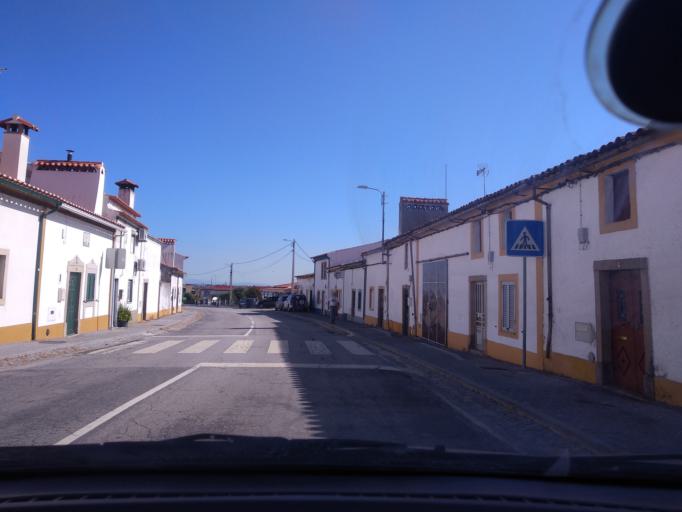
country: PT
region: Portalegre
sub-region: Nisa
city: Nisa
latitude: 39.4207
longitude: -7.6197
